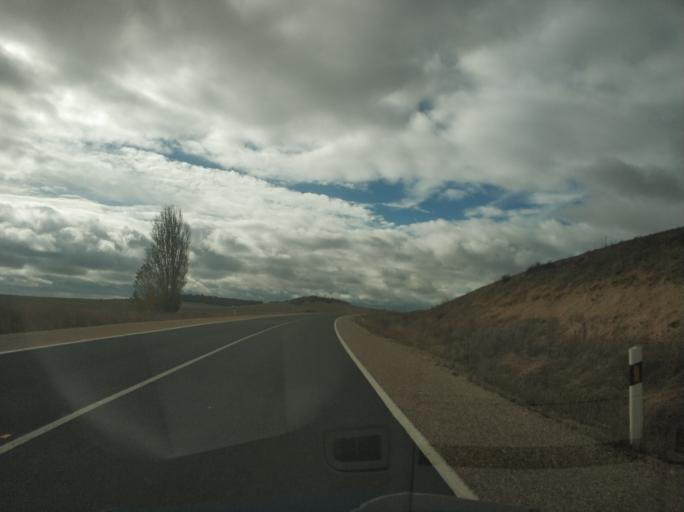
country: ES
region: Castille and Leon
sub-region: Provincia de Zamora
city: Castrillo de la Guarena
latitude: 41.2086
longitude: -5.3236
